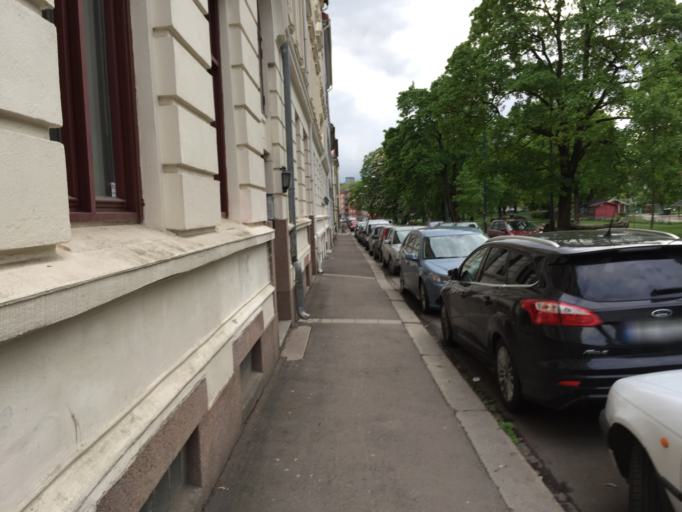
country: NO
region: Oslo
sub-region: Oslo
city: Oslo
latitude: 59.9218
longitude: 10.7655
